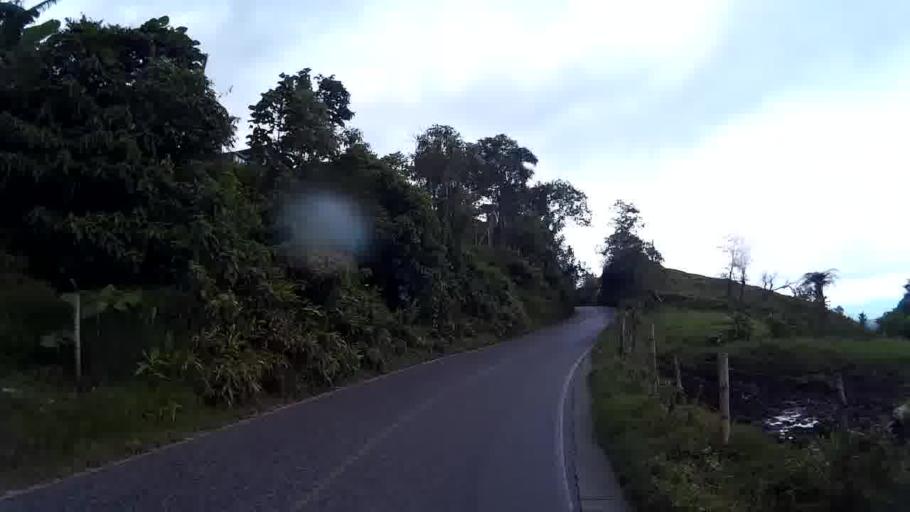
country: CO
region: Quindio
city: Filandia
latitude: 4.6784
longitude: -75.6582
